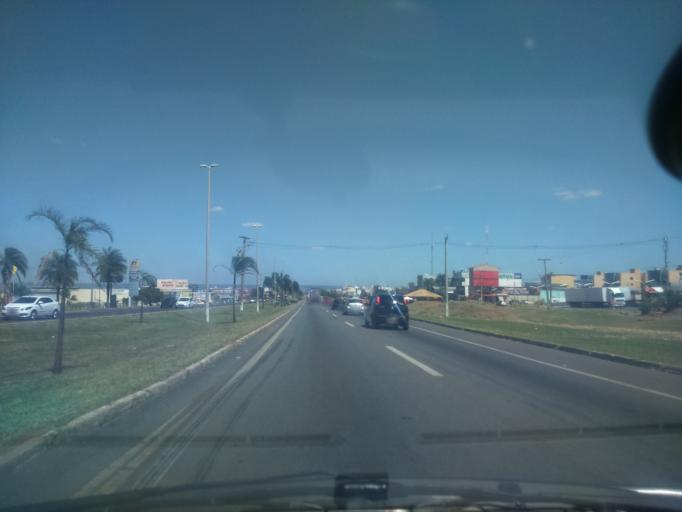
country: BR
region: Goias
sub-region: Luziania
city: Luziania
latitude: -16.0544
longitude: -47.9822
